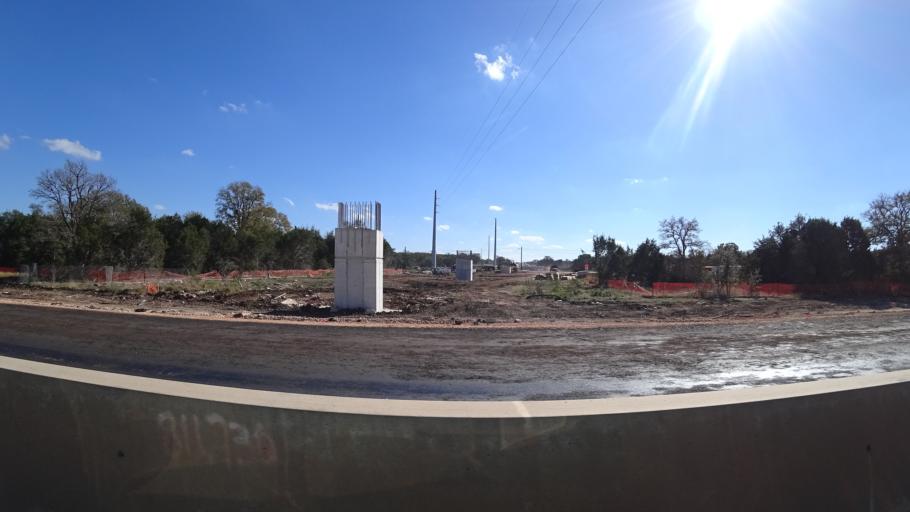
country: US
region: Texas
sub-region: Travis County
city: Shady Hollow
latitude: 30.1735
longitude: -97.8875
